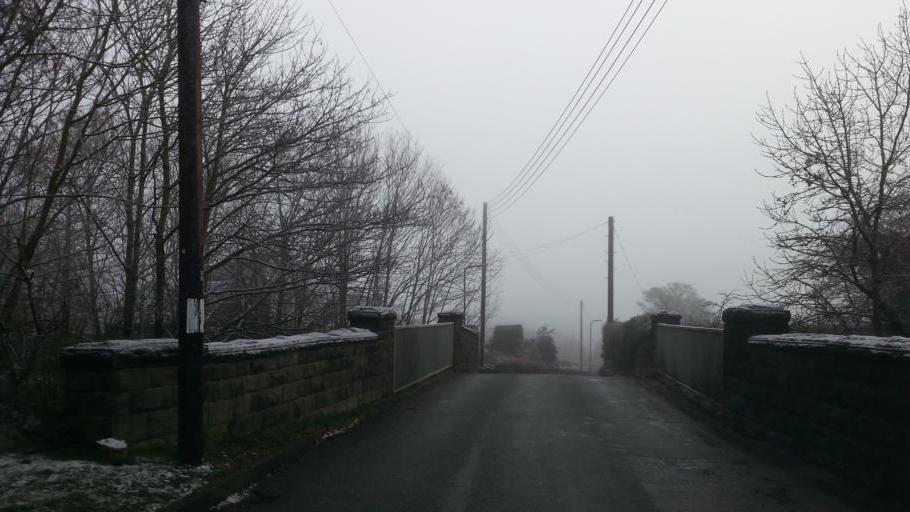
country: GB
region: England
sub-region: Staffordshire
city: Biddulph
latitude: 53.1249
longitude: -2.1752
